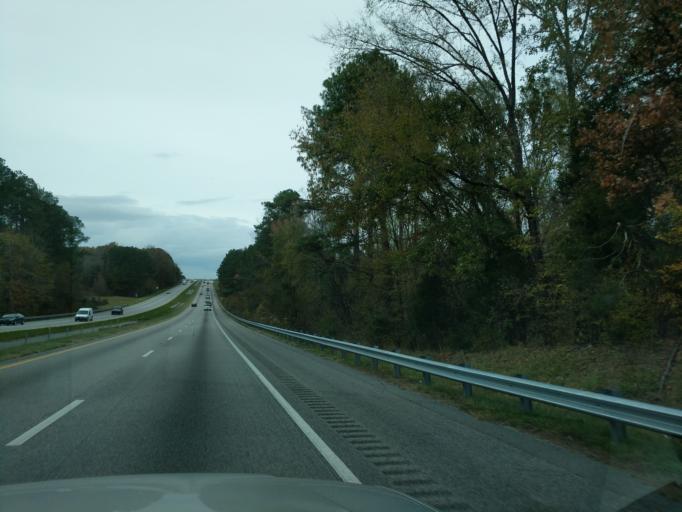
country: US
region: South Carolina
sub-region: Laurens County
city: Clinton
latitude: 34.4901
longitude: -81.8364
